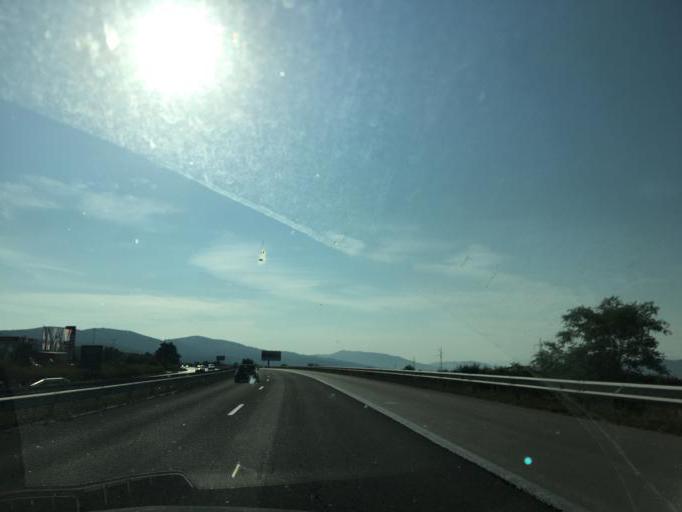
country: BG
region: Sofiya
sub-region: Obshtina Ikhtiman
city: Ikhtiman
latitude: 42.4780
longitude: 23.7964
